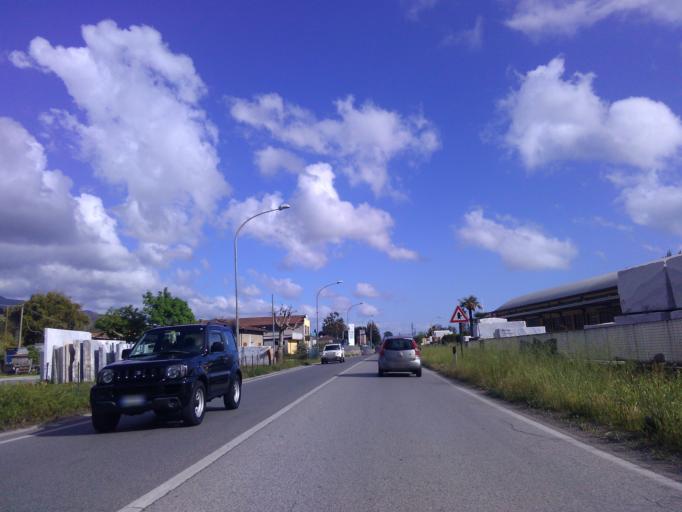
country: IT
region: Tuscany
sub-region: Provincia di Lucca
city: Strettoia
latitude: 43.9932
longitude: 10.1794
